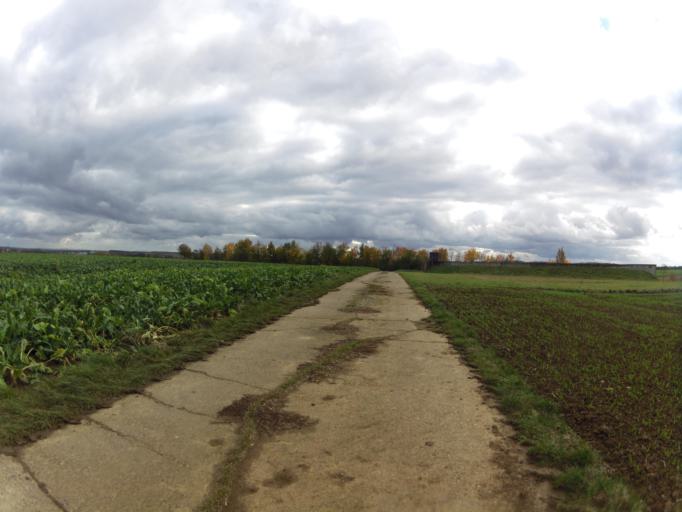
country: DE
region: Bavaria
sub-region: Regierungsbezirk Unterfranken
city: Kurnach
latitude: 49.8745
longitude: 10.0119
